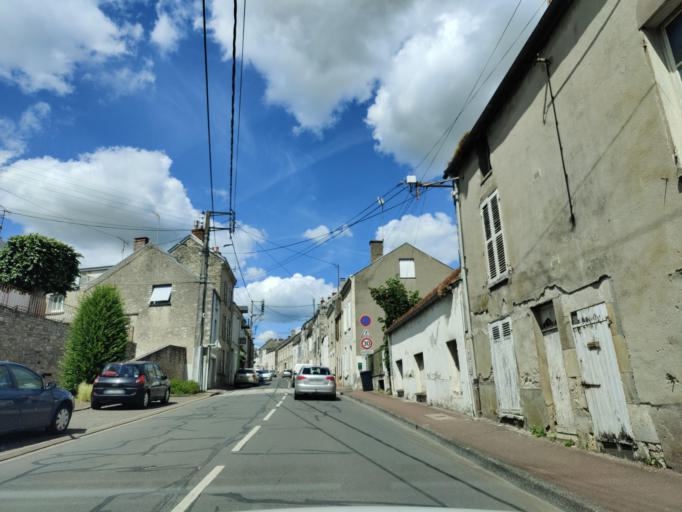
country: FR
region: Centre
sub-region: Departement du Loiret
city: Pithiviers
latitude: 48.1682
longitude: 2.2564
